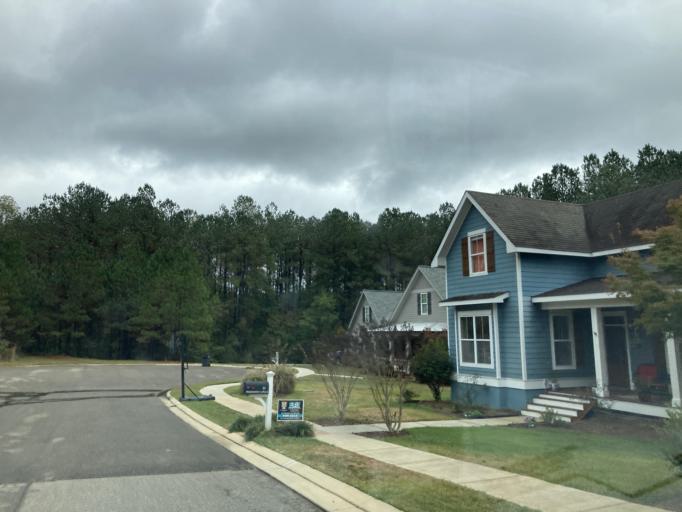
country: US
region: Mississippi
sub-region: Lamar County
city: West Hattiesburg
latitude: 31.2868
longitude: -89.4728
